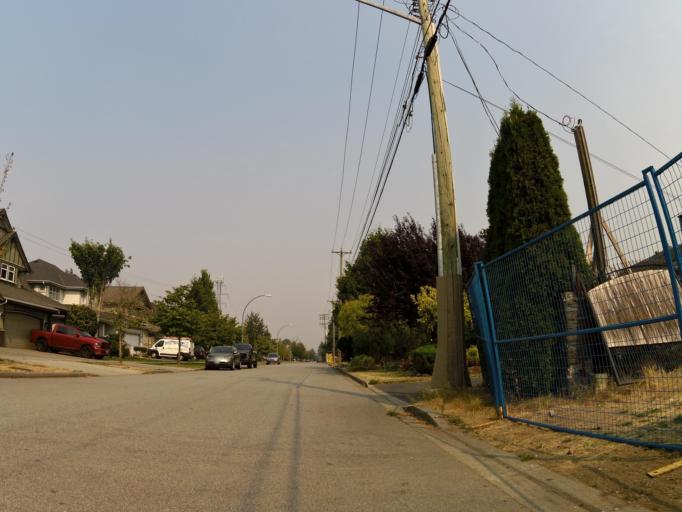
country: CA
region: British Columbia
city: Delta
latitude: 49.1525
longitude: -122.9234
